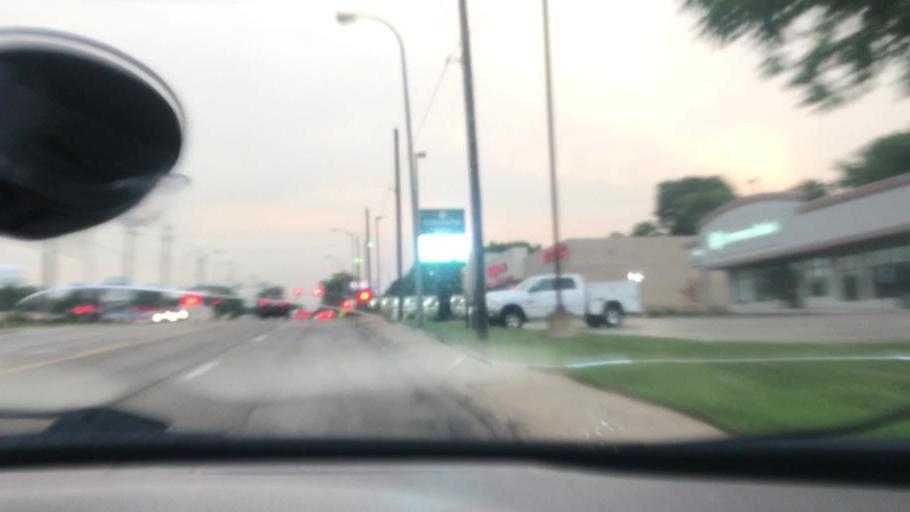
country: US
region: Illinois
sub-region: Tazewell County
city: Pekin
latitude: 40.5596
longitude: -89.6187
